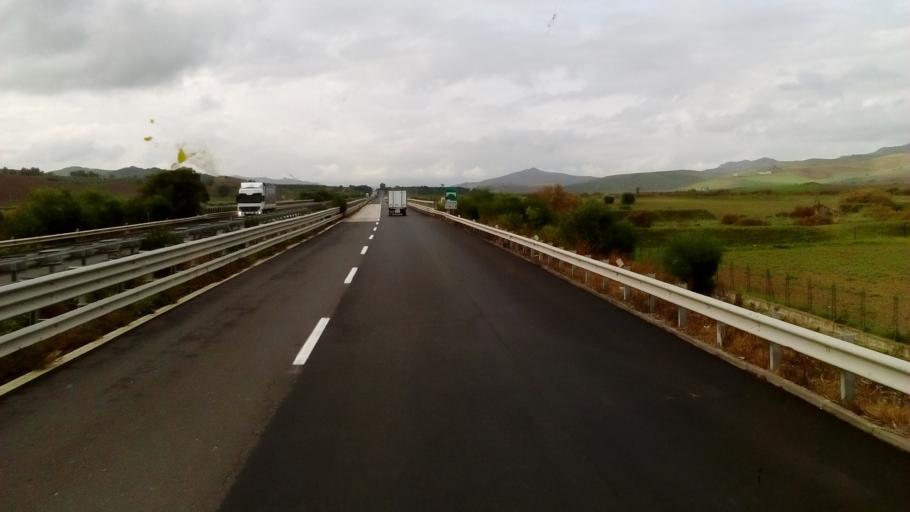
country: IT
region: Sicily
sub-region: Enna
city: Catenanuova
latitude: 37.5687
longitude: 14.6390
